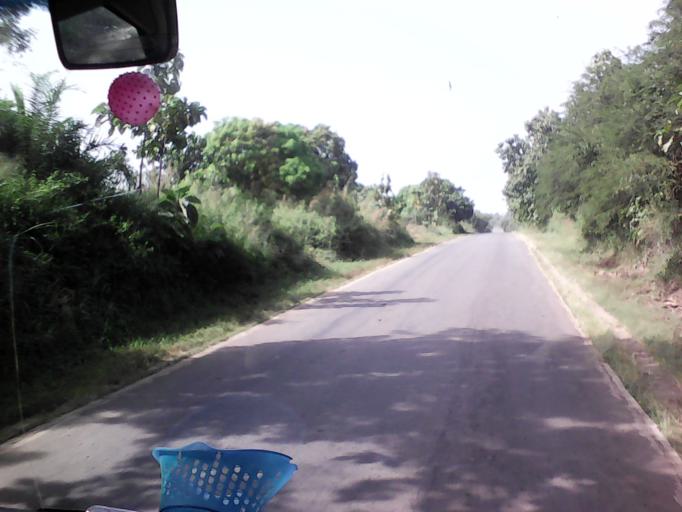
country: TG
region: Centrale
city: Sokode
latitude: 8.9060
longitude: 1.0940
